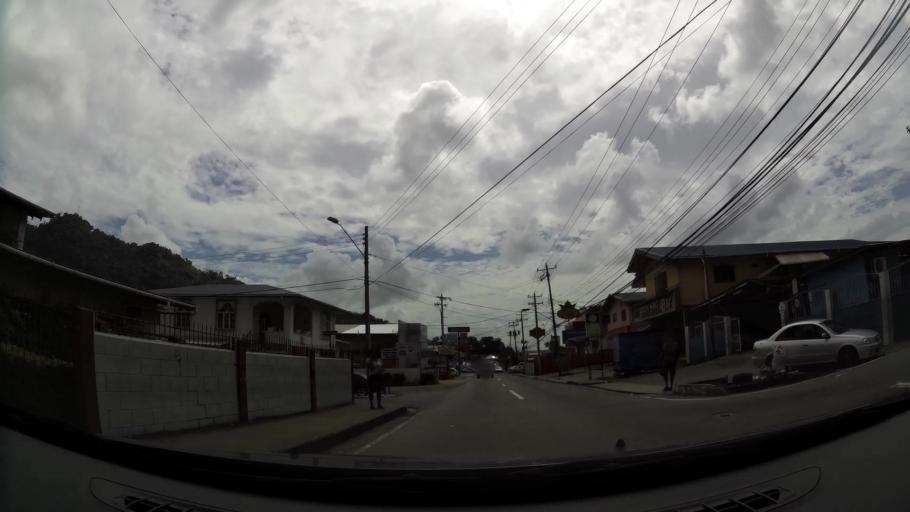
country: TT
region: Diego Martin
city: Petit Valley
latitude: 10.6925
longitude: -61.5549
